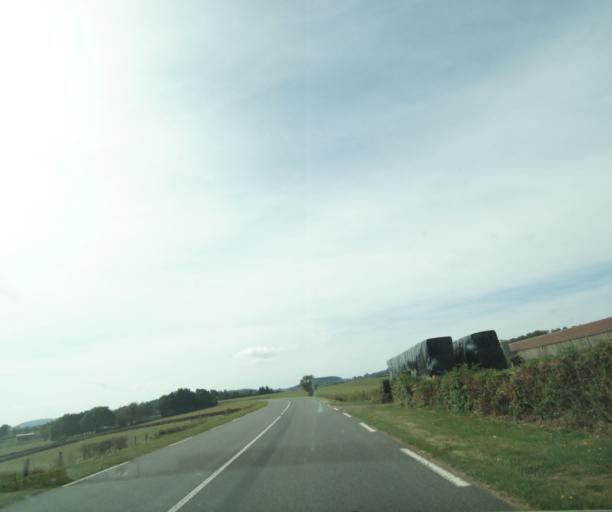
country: FR
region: Auvergne
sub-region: Departement de l'Allier
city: Le Donjon
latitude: 46.3296
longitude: 3.7684
